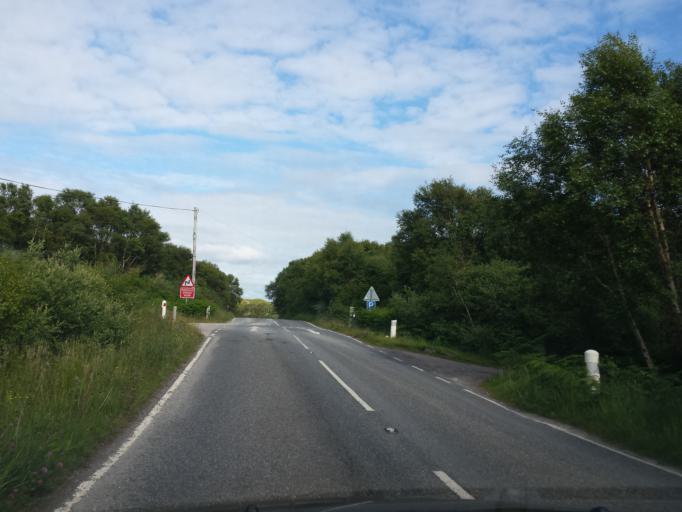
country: GB
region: Scotland
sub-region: Argyll and Bute
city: Isle Of Mull
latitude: 56.9614
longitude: -5.8261
